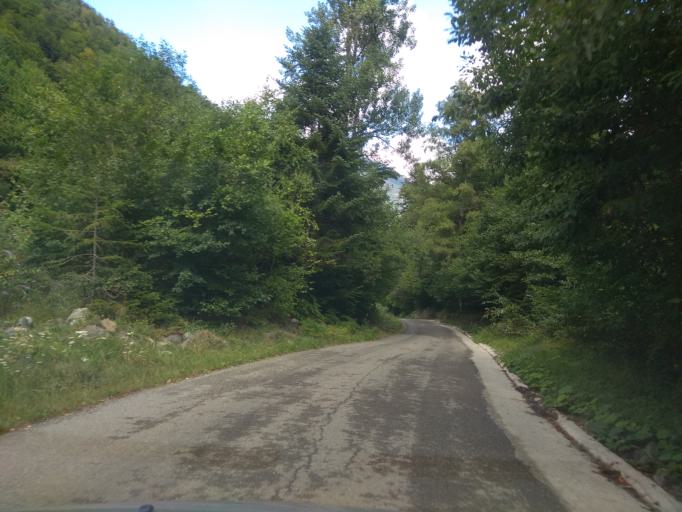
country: ES
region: Catalonia
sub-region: Provincia de Lleida
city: Vielha
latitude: 42.7206
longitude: 0.7241
